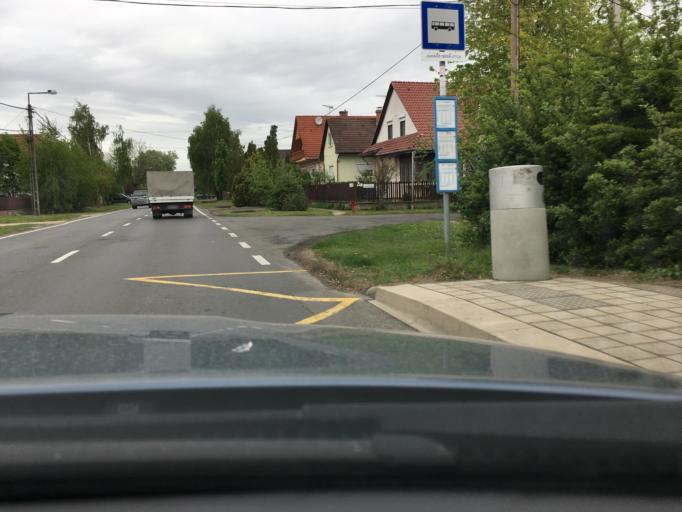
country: HU
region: Hajdu-Bihar
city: Debrecen
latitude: 47.5469
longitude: 21.6714
